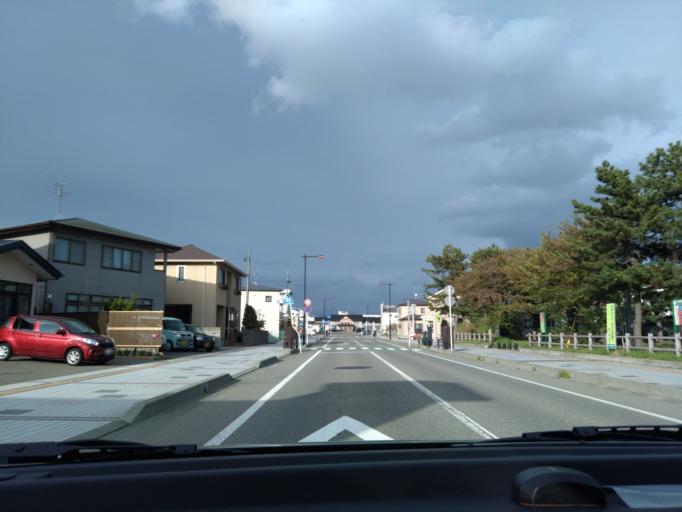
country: JP
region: Akita
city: Akita Shi
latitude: 39.7577
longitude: 140.0713
